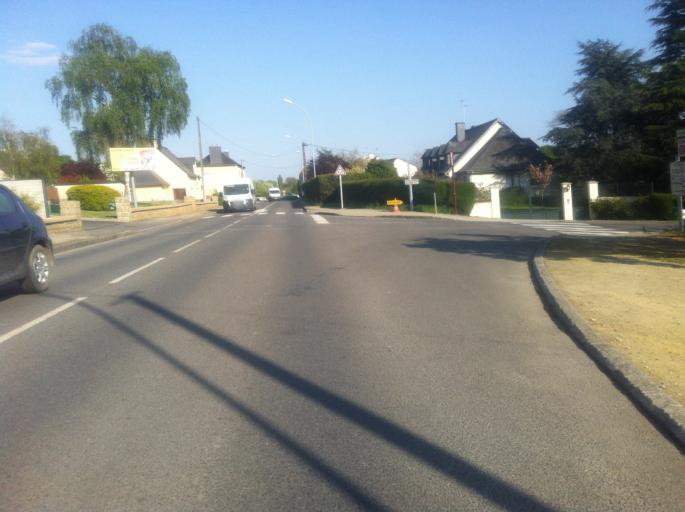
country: FR
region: Brittany
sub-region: Departement d'Ille-et-Vilaine
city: Bruz
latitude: 48.0210
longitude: -1.7296
